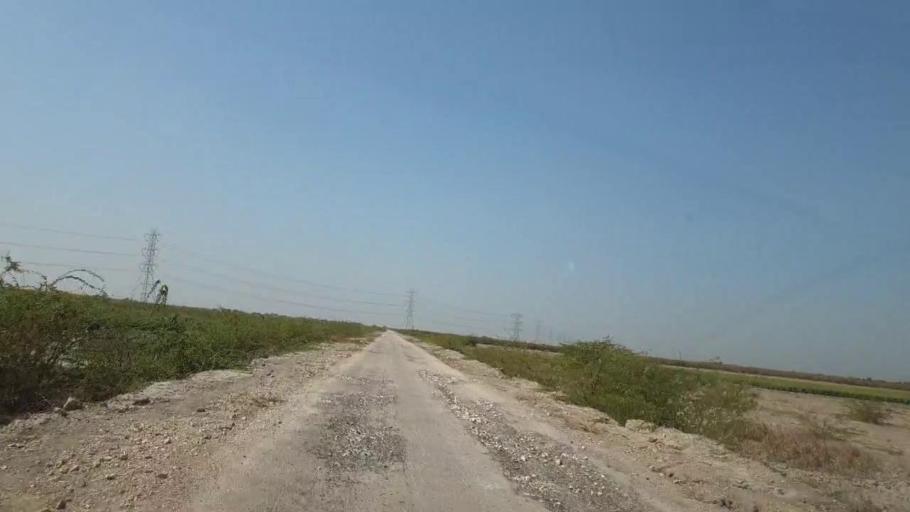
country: PK
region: Sindh
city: Kunri
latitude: 25.0965
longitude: 69.4885
